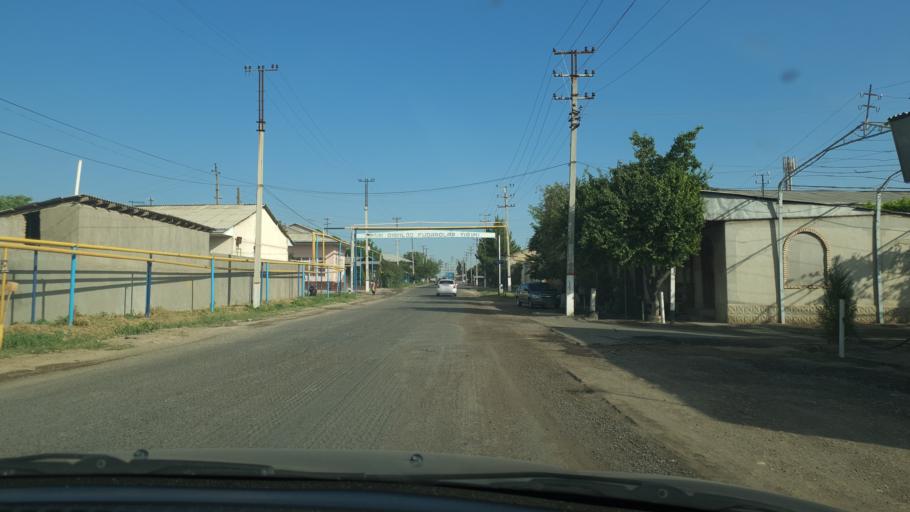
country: UZ
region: Toshkent
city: Urtaowul
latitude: 41.2055
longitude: 69.1503
